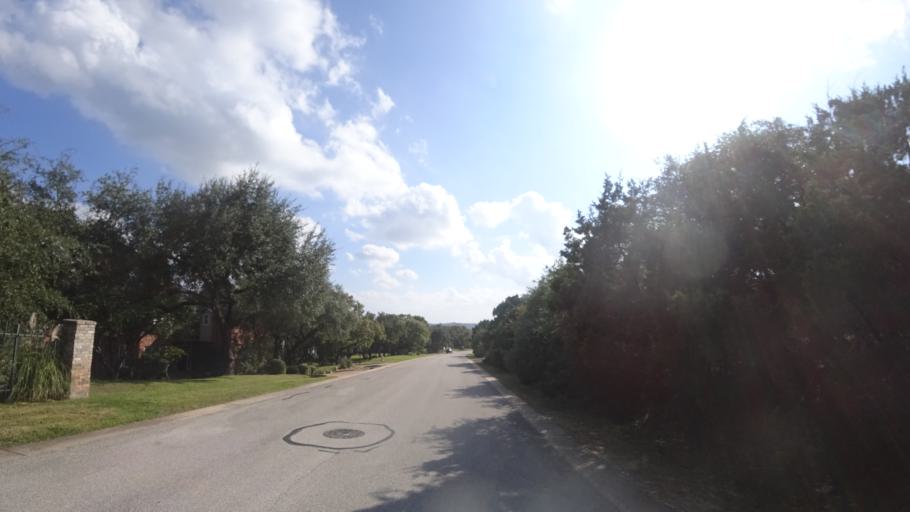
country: US
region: Texas
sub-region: Travis County
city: Lost Creek
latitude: 30.3043
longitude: -97.8510
